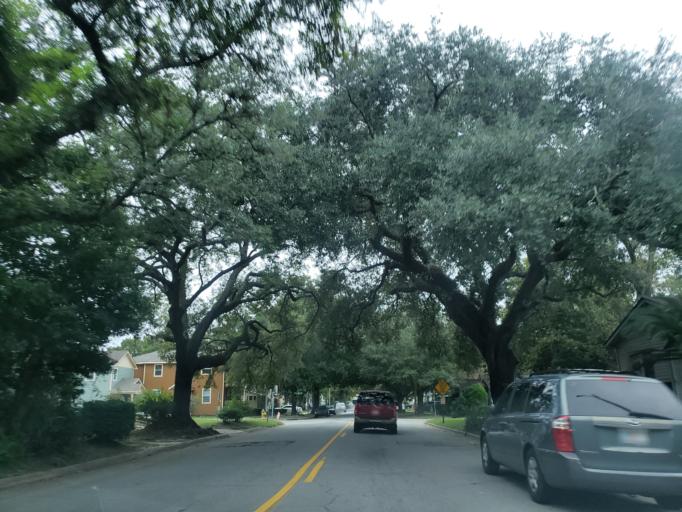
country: US
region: Georgia
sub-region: Chatham County
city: Savannah
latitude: 32.0524
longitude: -81.0825
